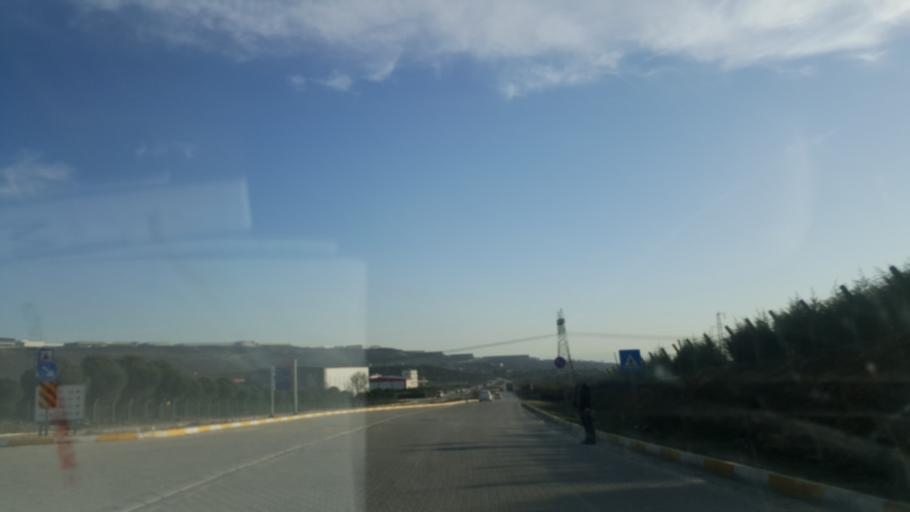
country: TR
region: Kocaeli
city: Tavsanli
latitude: 40.8638
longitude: 29.5593
